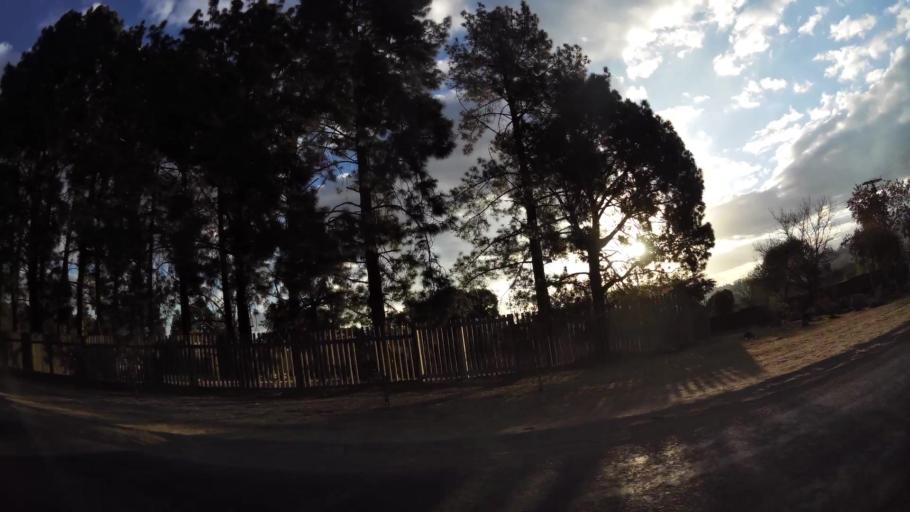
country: ZA
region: Gauteng
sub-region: City of Johannesburg Metropolitan Municipality
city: Midrand
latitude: -25.9512
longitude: 28.1542
